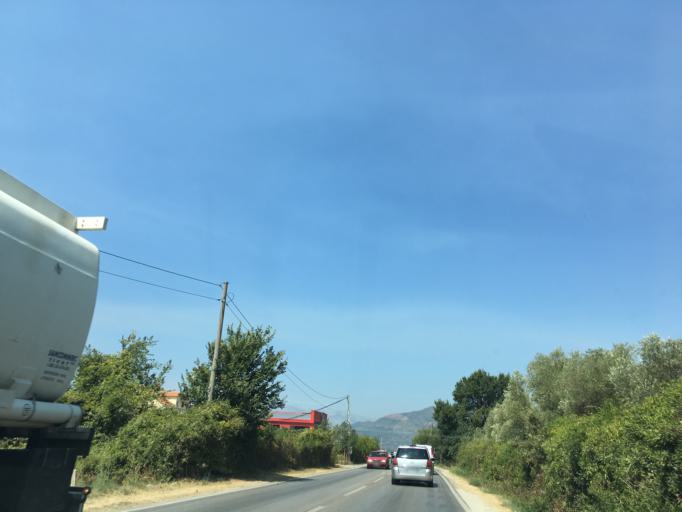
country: ME
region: Kotor
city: Kotor
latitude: 42.3742
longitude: 18.7525
